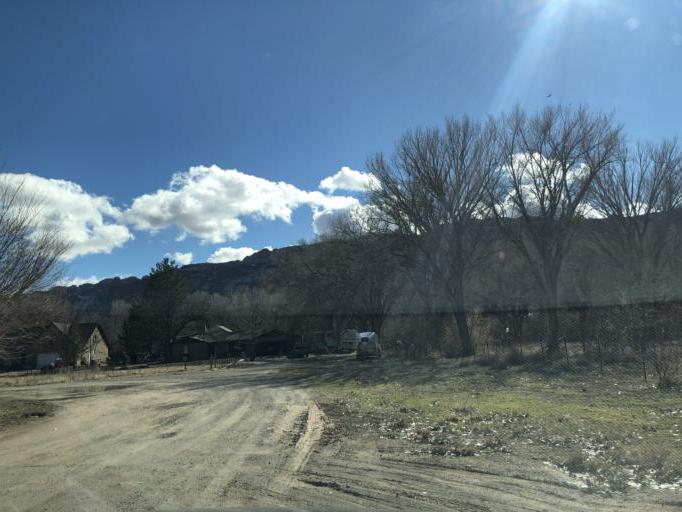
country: US
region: Utah
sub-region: Grand County
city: Moab
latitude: 38.5738
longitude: -109.5566
